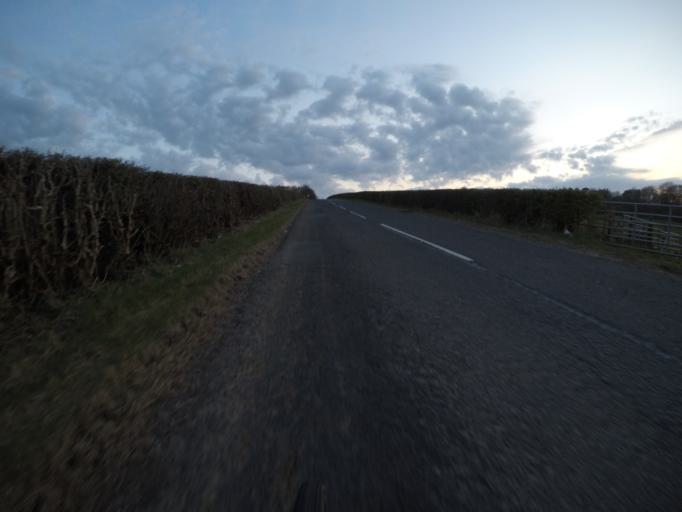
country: GB
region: Scotland
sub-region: South Ayrshire
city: Dundonald
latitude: 55.5711
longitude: -4.5953
